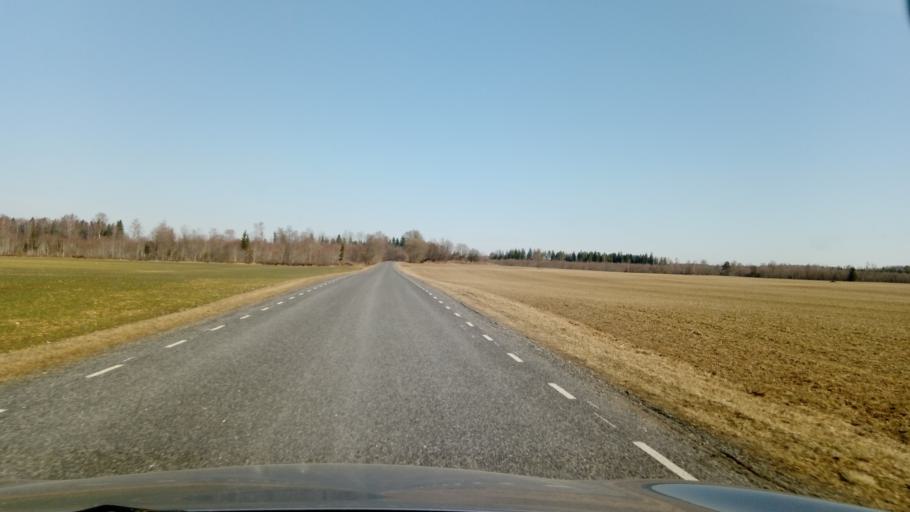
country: EE
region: Laeaene-Virumaa
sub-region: Tamsalu vald
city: Tamsalu
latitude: 59.1799
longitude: 26.1274
